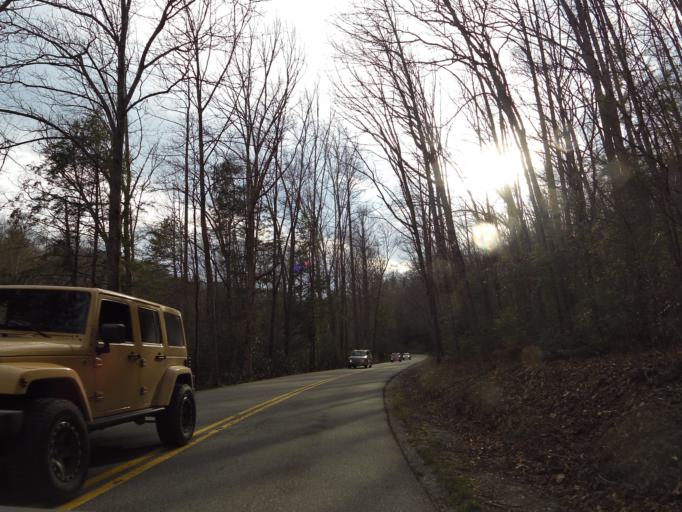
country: US
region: Tennessee
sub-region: Sevier County
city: Gatlinburg
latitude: 35.6657
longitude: -83.6029
